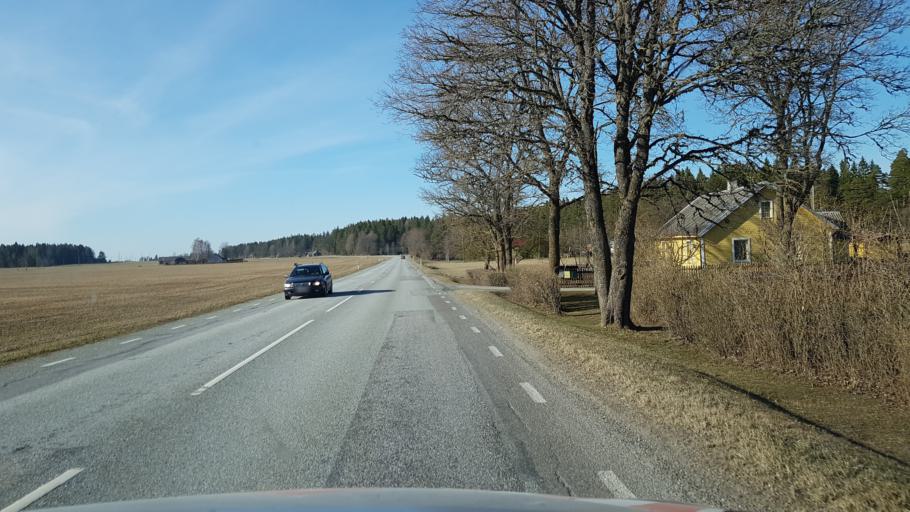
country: EE
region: Laeaene-Virumaa
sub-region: Vinni vald
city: Vinni
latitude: 59.1826
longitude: 26.5768
